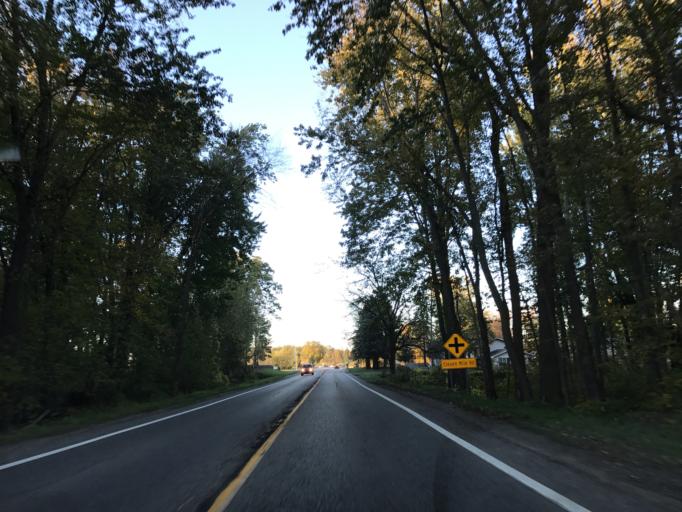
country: US
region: Michigan
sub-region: Oakland County
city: South Lyon
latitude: 42.4739
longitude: -83.6131
